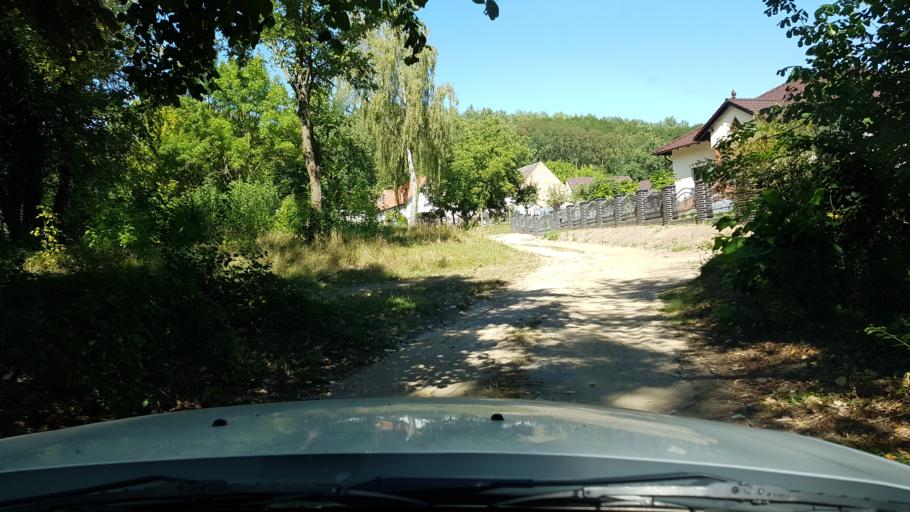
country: PL
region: West Pomeranian Voivodeship
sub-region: Powiat gryfinski
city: Cedynia
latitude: 52.8341
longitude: 14.1918
